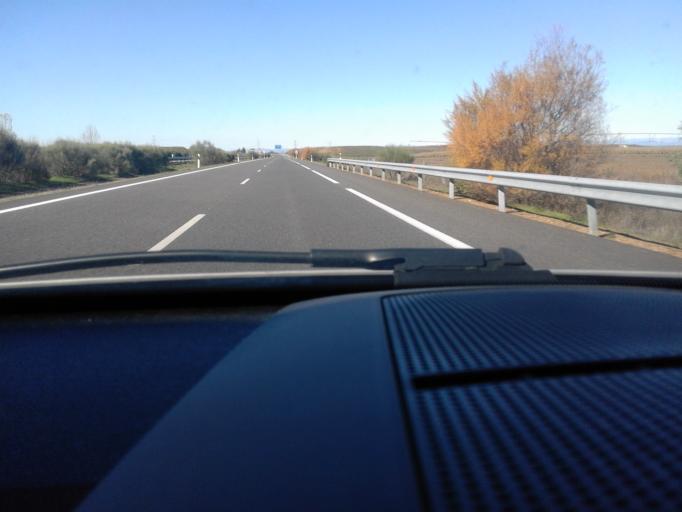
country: ES
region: Castille and Leon
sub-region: Provincia de Leon
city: Santas Martas
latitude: 42.4402
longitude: -5.3516
